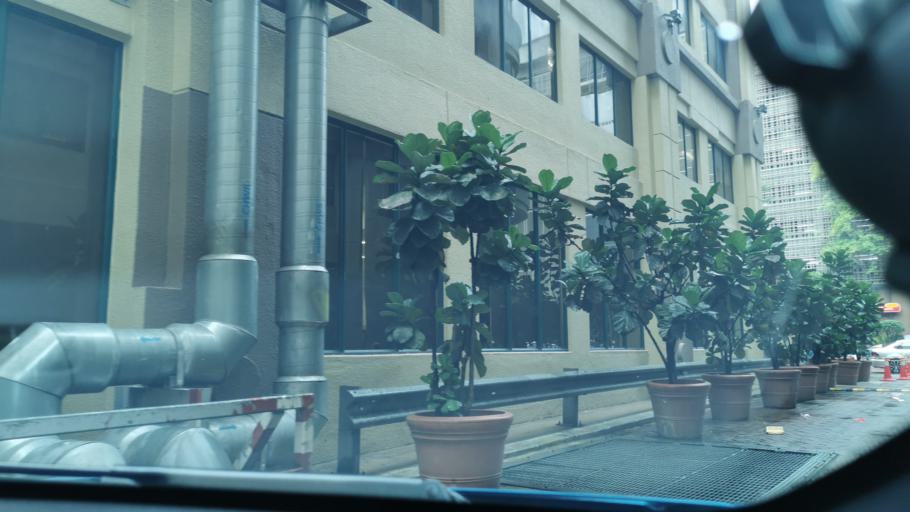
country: MY
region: Kuala Lumpur
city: Kuala Lumpur
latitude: 3.1176
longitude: 101.6760
